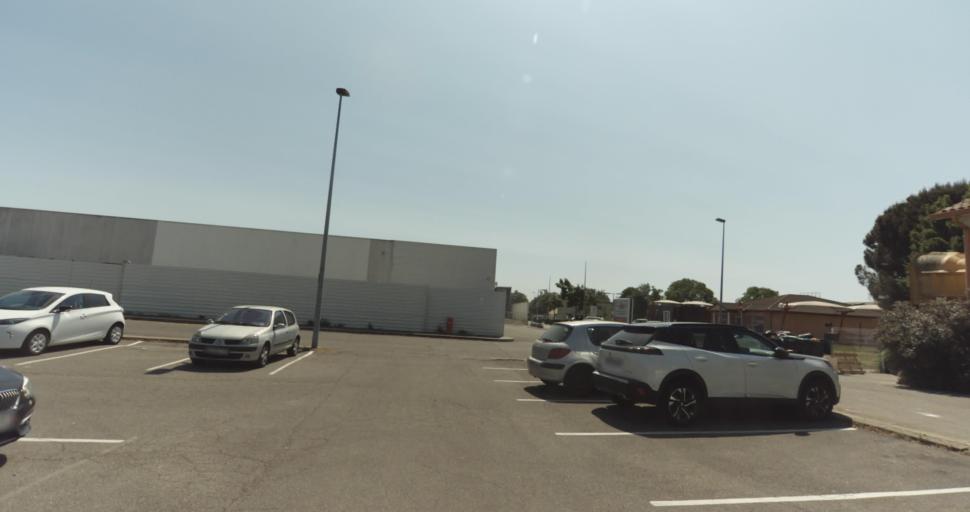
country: FR
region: Midi-Pyrenees
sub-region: Departement de la Haute-Garonne
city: Plaisance-du-Touch
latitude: 43.5689
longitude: 1.3080
